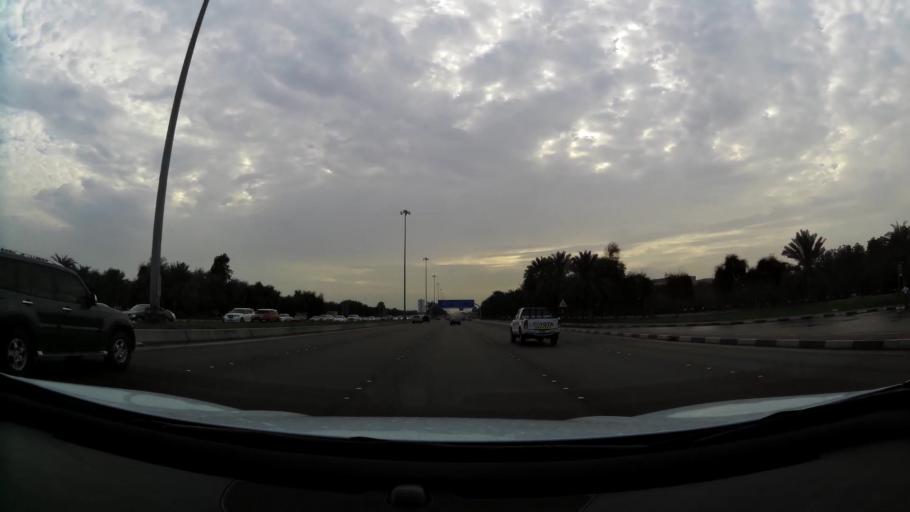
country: AE
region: Abu Dhabi
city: Abu Dhabi
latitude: 24.4001
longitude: 54.4974
